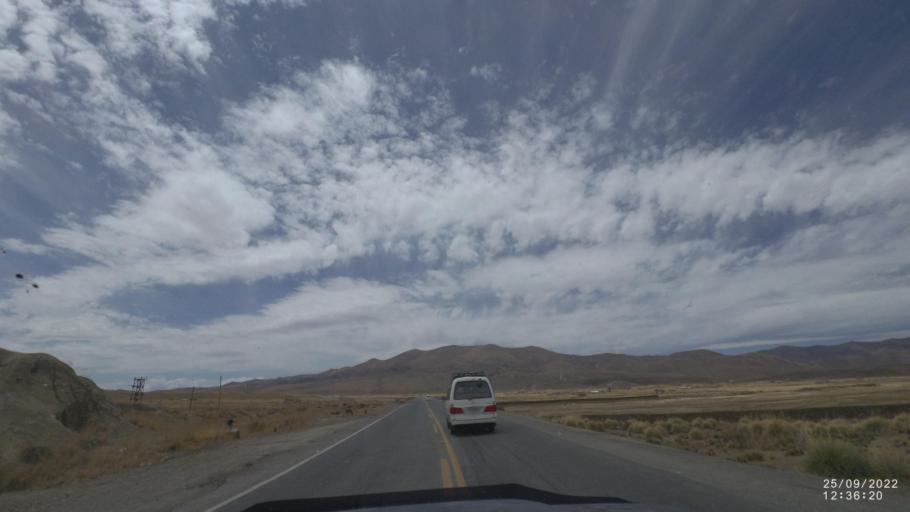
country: BO
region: Oruro
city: Machacamarca
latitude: -18.1654
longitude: -66.9895
